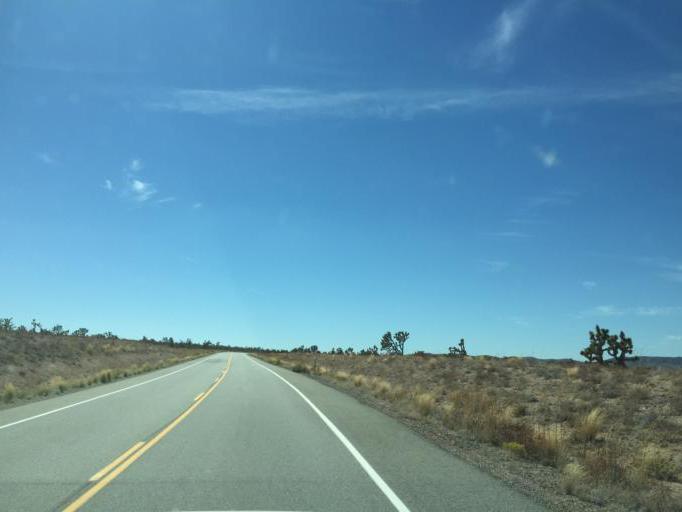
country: US
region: Arizona
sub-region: Mohave County
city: Meadview
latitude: 35.8902
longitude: -114.0365
